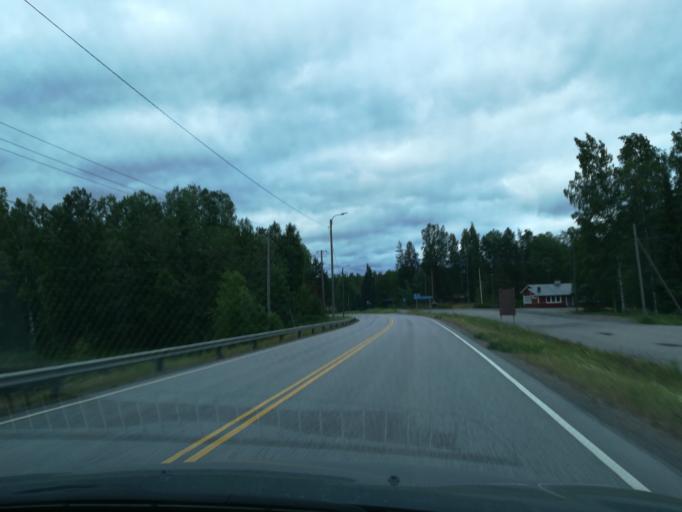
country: FI
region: Southern Savonia
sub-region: Mikkeli
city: Ristiina
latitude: 61.3542
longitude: 27.3994
